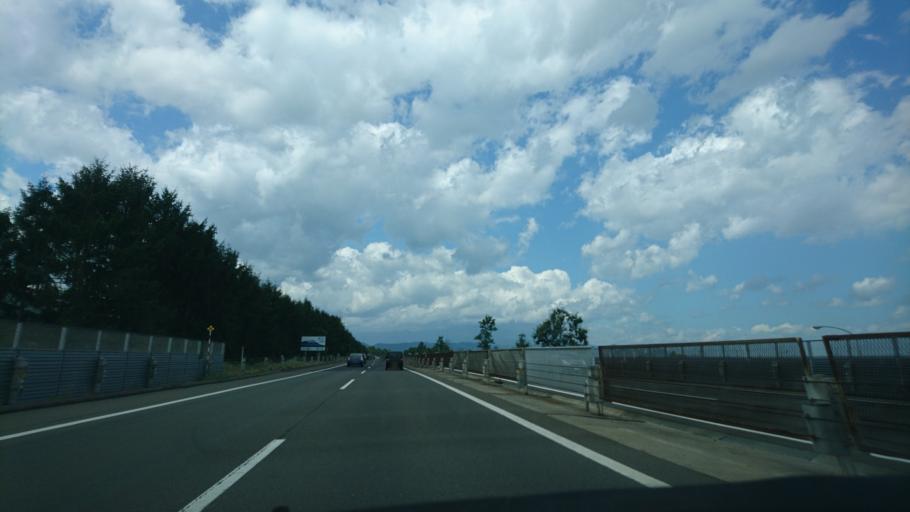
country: JP
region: Iwate
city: Morioka-shi
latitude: 39.6638
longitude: 141.1142
